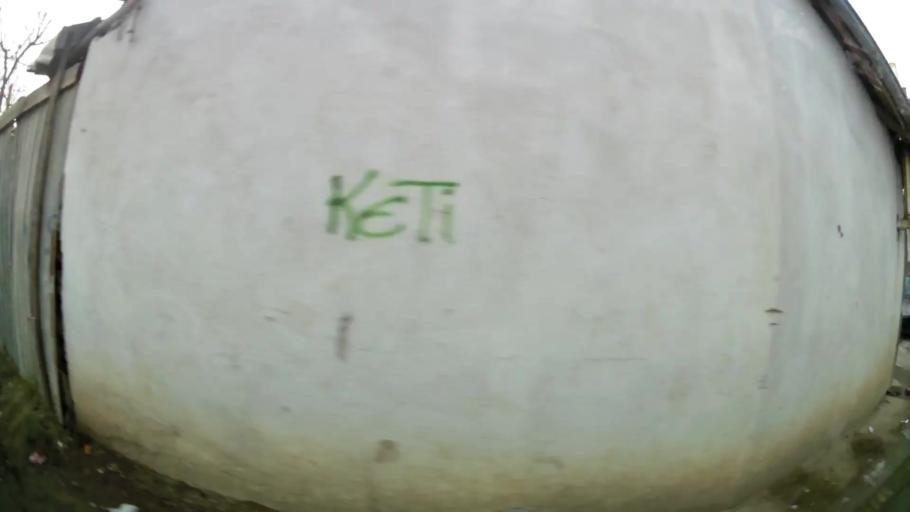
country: MK
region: Suto Orizari
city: Suto Orizare
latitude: 42.0329
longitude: 21.4212
